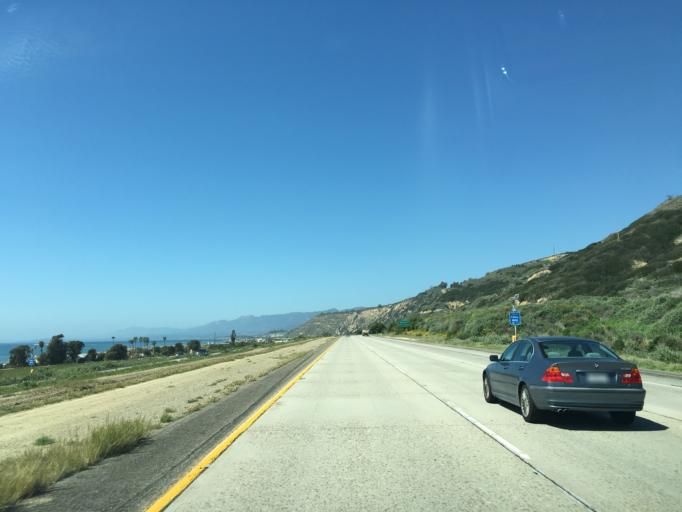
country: US
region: California
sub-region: Ventura County
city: Oak View
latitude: 34.3391
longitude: -119.4087
